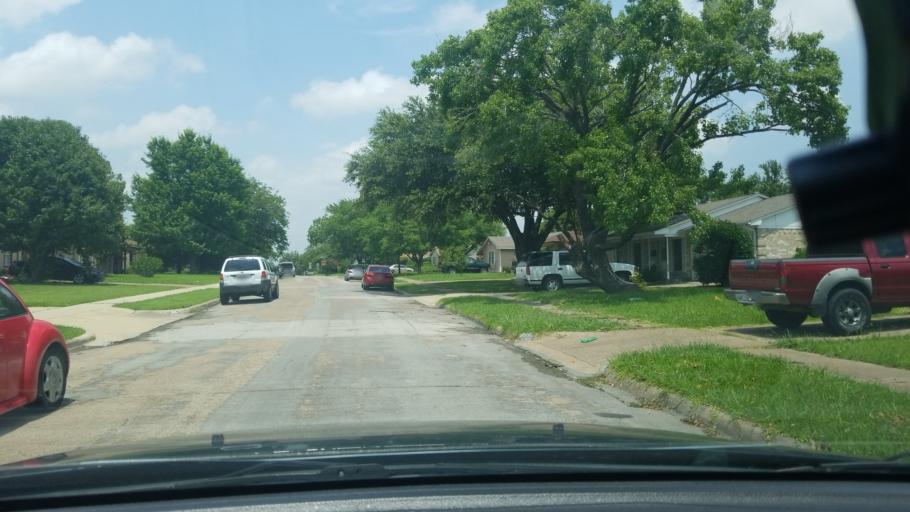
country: US
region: Texas
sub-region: Dallas County
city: Mesquite
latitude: 32.7972
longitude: -96.6397
